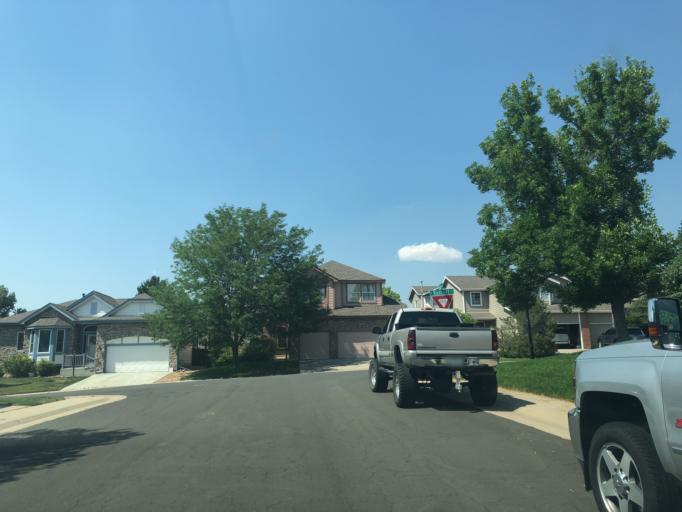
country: US
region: Colorado
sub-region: Arapahoe County
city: Dove Valley
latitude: 39.6359
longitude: -104.7714
